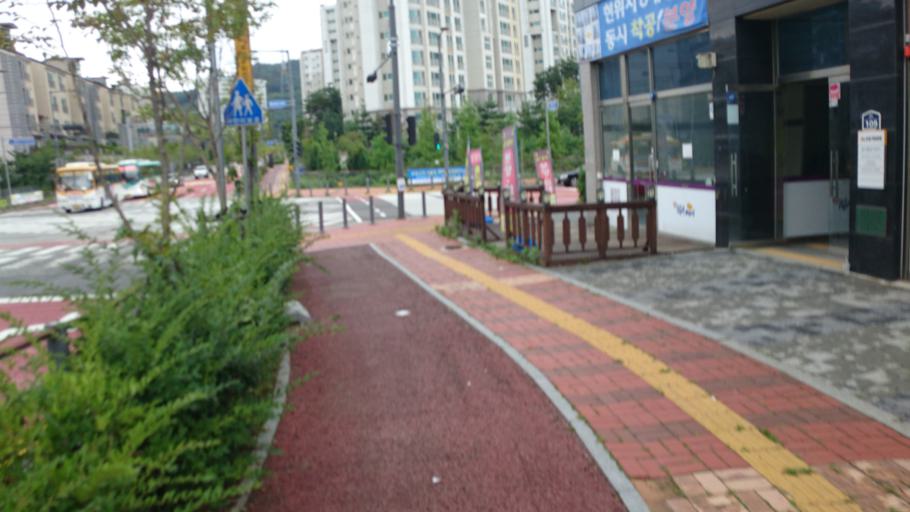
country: KR
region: Gyeonggi-do
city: Suwon-si
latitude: 37.3053
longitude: 127.0471
